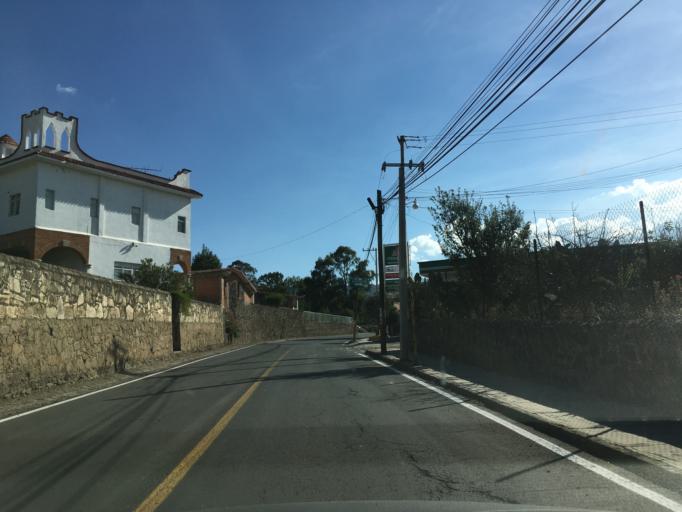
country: MX
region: Hidalgo
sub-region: Omitlan de Juarez
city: San Antonio el Paso
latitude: 20.2055
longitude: -98.5716
